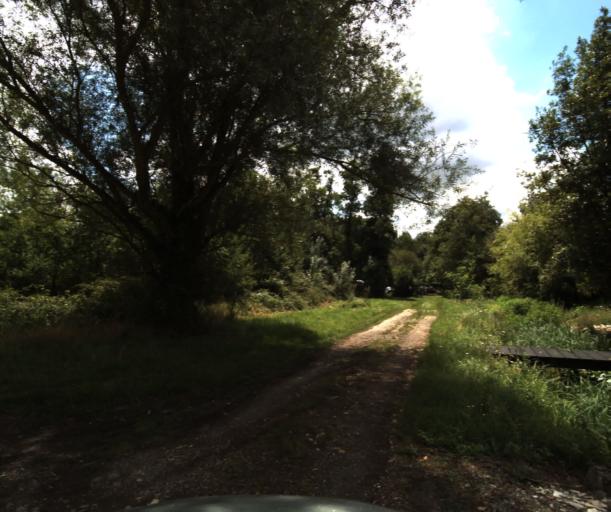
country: FR
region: Midi-Pyrenees
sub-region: Departement de la Haute-Garonne
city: Lacasse
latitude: 43.3971
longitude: 1.2704
